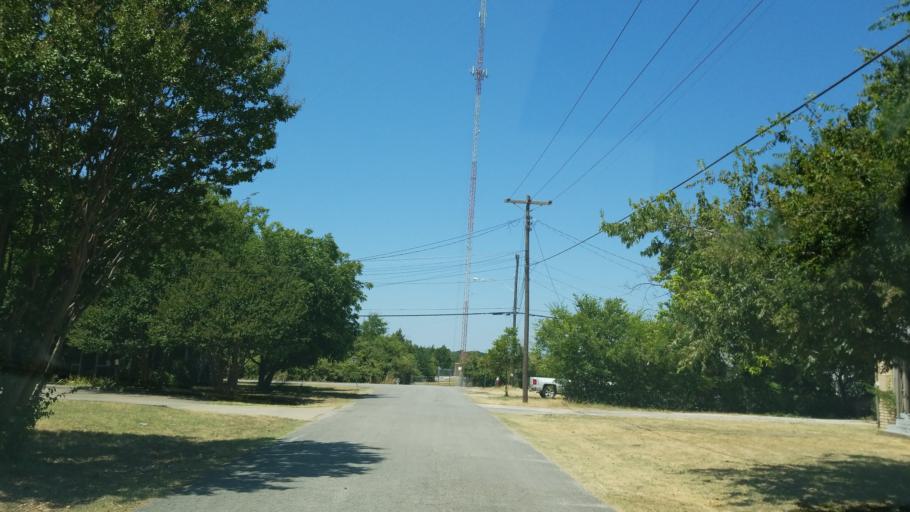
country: US
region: Texas
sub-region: Dallas County
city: Cockrell Hill
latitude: 32.7411
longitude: -96.8933
